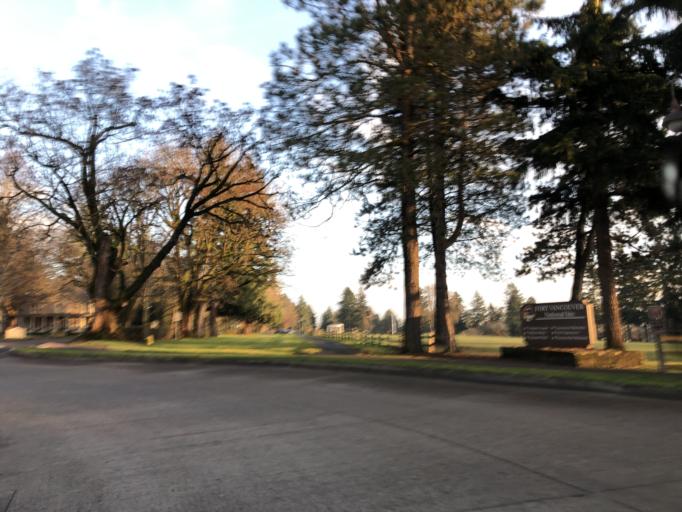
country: US
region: Washington
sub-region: Clark County
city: Vancouver
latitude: 45.6286
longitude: -122.6632
